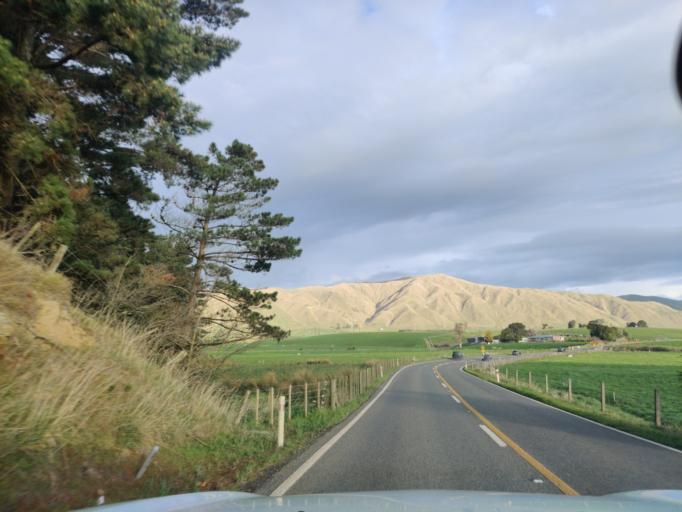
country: NZ
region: Manawatu-Wanganui
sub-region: Palmerston North City
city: Palmerston North
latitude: -40.4943
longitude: 175.4932
